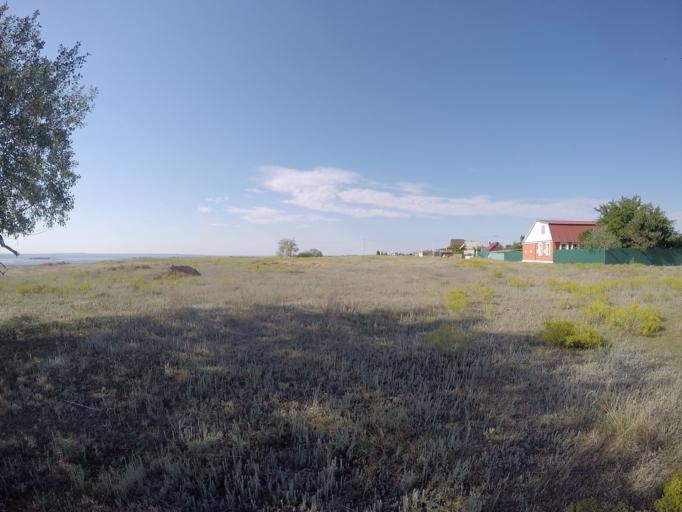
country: RU
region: Saratov
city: Privolzhskiy
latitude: 51.2003
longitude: 45.9101
